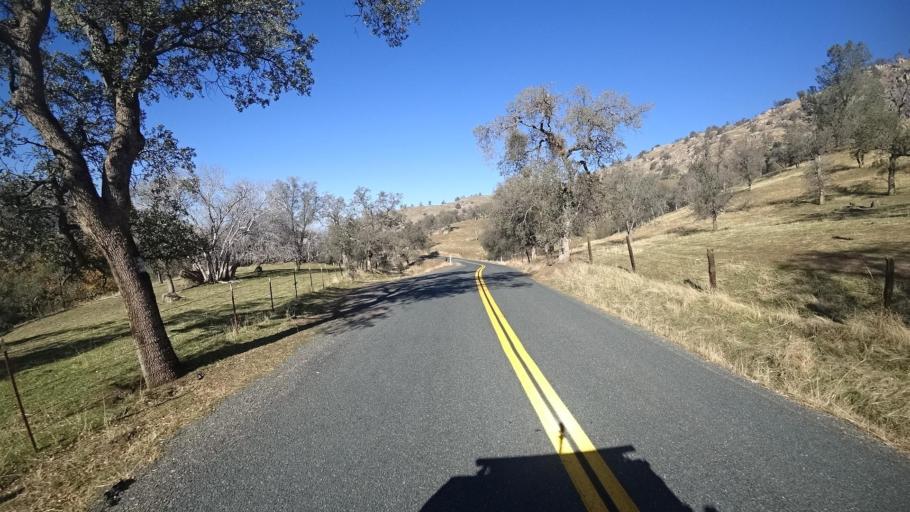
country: US
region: California
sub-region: Kern County
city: Alta Sierra
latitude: 35.7883
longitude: -118.7919
